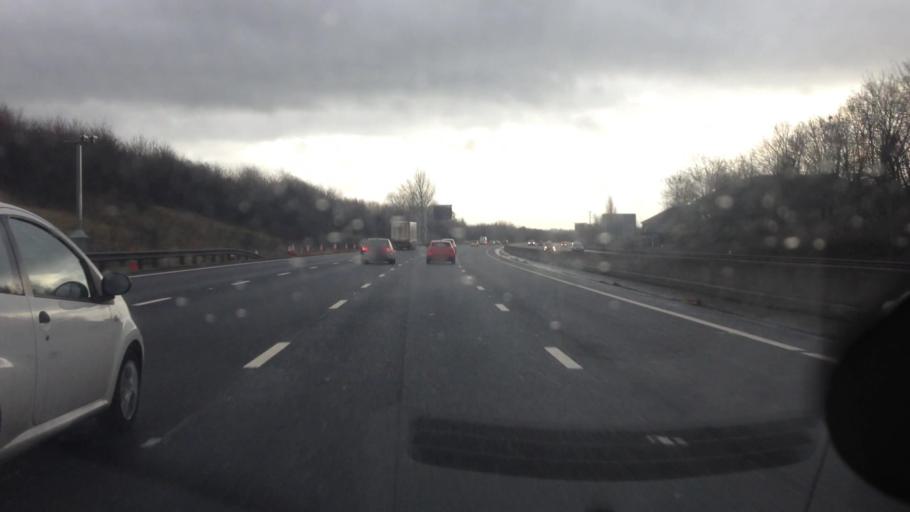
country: GB
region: England
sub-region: City and Borough of Wakefield
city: Horbury
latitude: 53.6679
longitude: -1.5424
